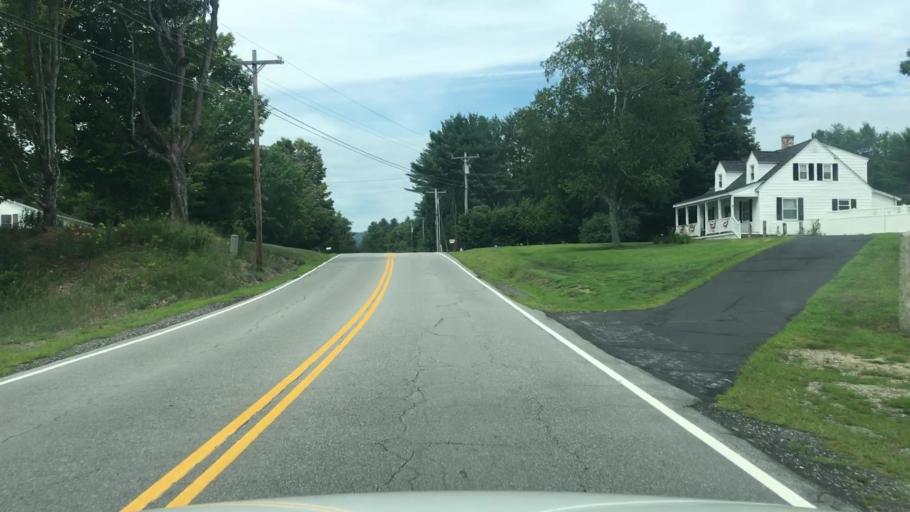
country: US
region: New Hampshire
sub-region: Grafton County
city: Rumney
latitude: 43.7859
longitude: -71.7716
